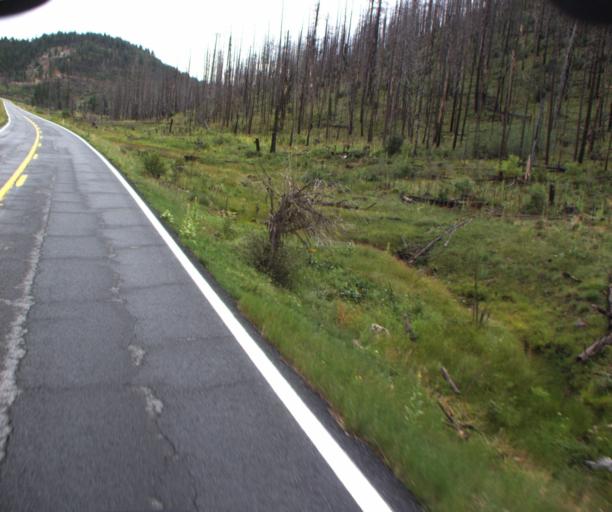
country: US
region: Arizona
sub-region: Apache County
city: Eagar
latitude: 33.7968
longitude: -109.1545
